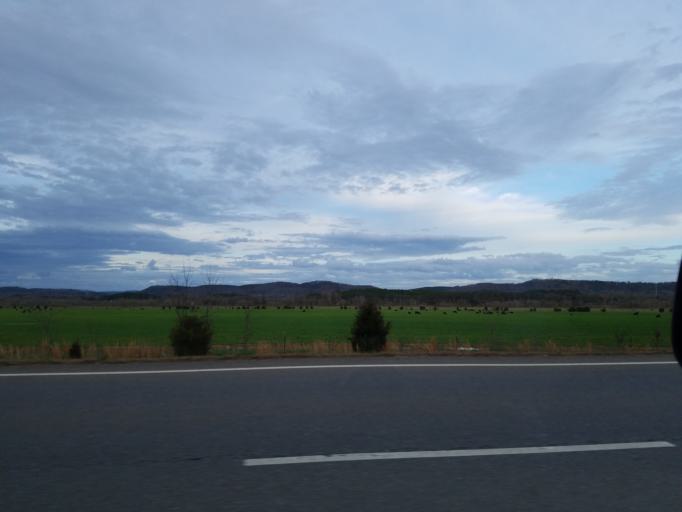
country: US
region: Georgia
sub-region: Bartow County
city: Rydal
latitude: 34.4448
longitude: -84.7240
